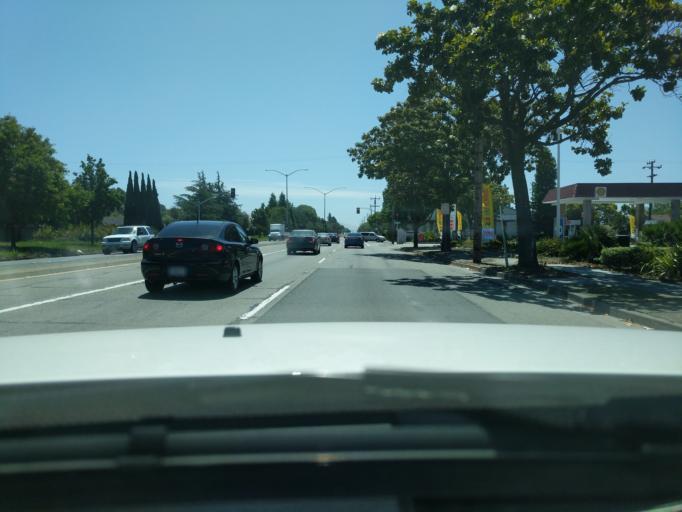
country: US
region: California
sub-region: Alameda County
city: Union City
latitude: 37.6192
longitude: -122.0350
